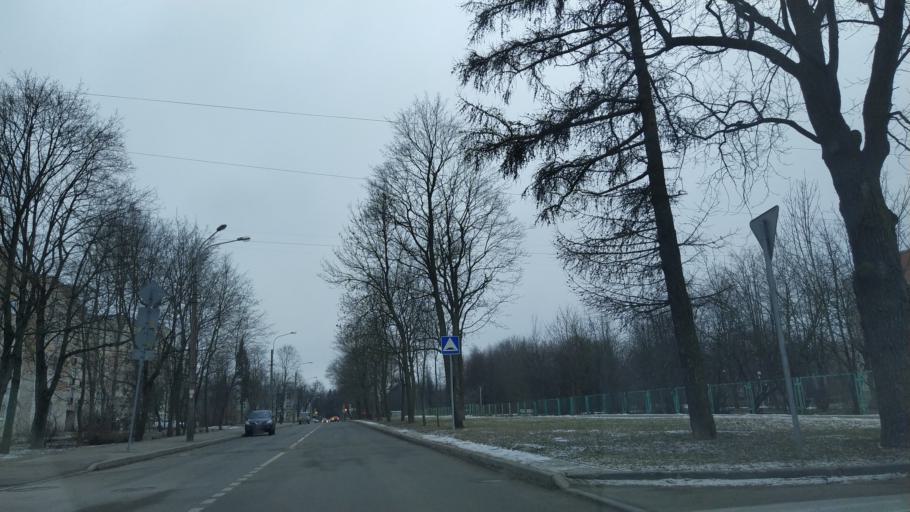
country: RU
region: St.-Petersburg
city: Pushkin
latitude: 59.7287
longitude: 30.4037
